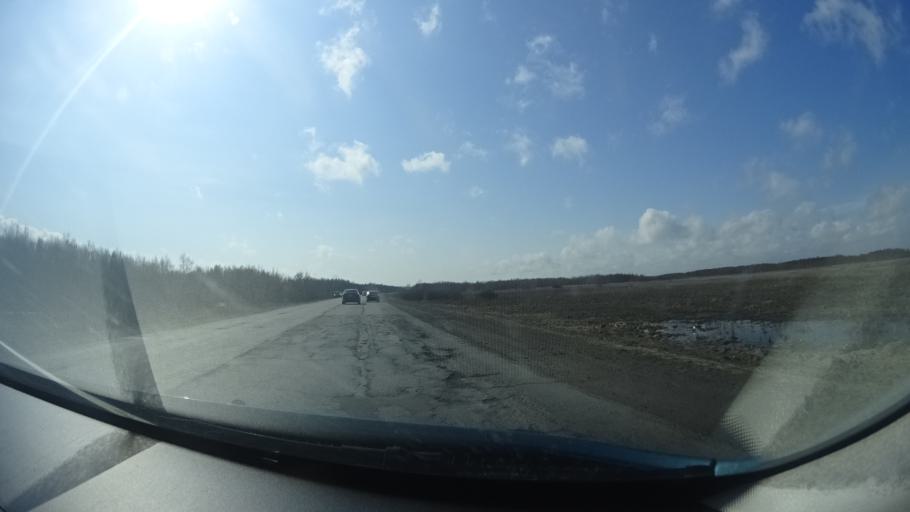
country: RU
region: Bashkortostan
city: Mikhaylovka
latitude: 54.9162
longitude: 55.7350
